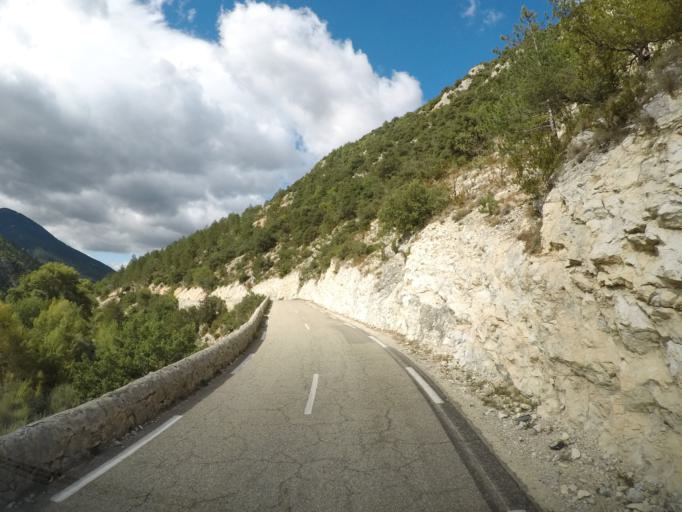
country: FR
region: Rhone-Alpes
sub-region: Departement de la Drome
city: Buis-les-Baronnies
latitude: 44.1880
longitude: 5.3435
